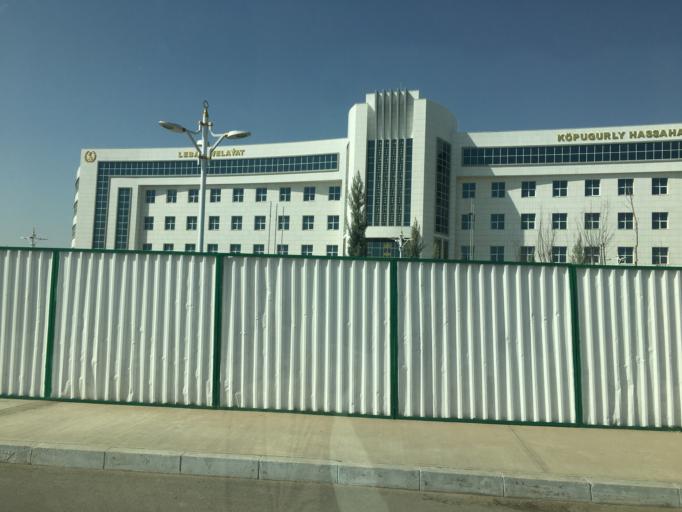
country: TM
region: Lebap
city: Turkmenabat
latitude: 39.0147
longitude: 63.5998
